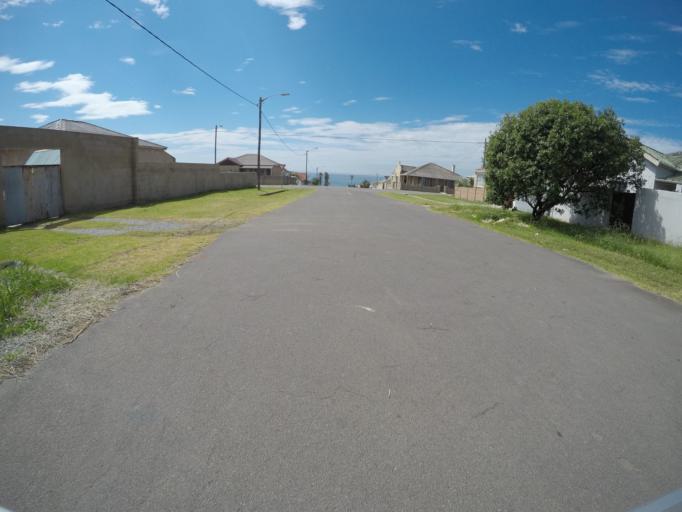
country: ZA
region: Eastern Cape
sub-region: Buffalo City Metropolitan Municipality
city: East London
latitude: -33.0368
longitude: 27.9035
